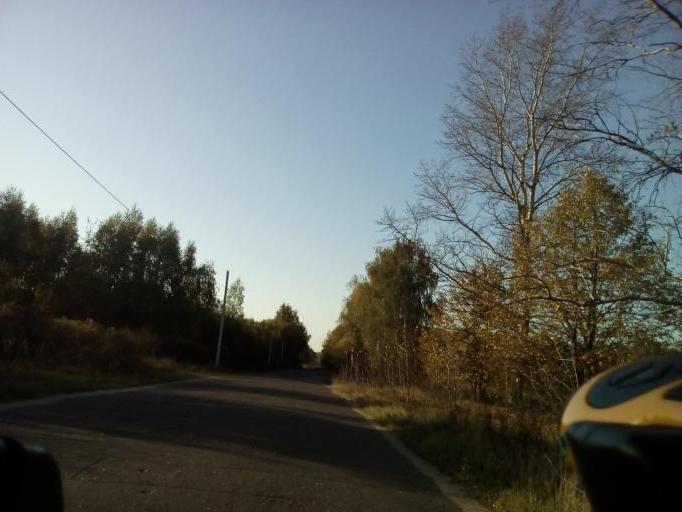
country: RU
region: Moskovskaya
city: Gzhel'
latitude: 55.6046
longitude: 38.3080
